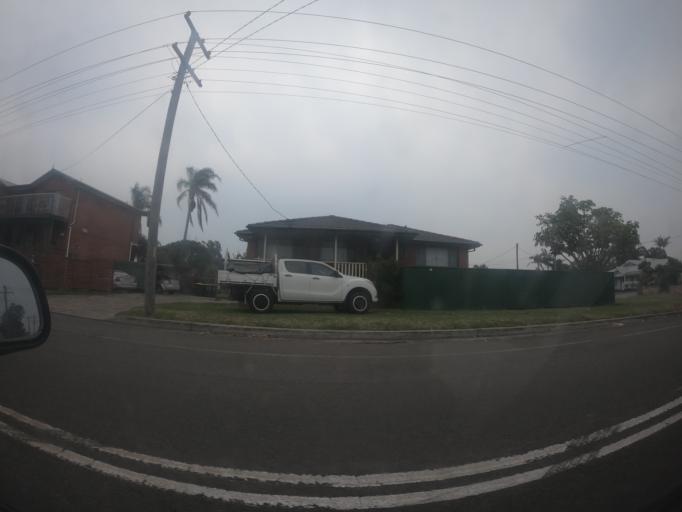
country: AU
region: New South Wales
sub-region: Shellharbour
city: Barrack Heights
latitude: -34.5649
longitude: 150.8676
